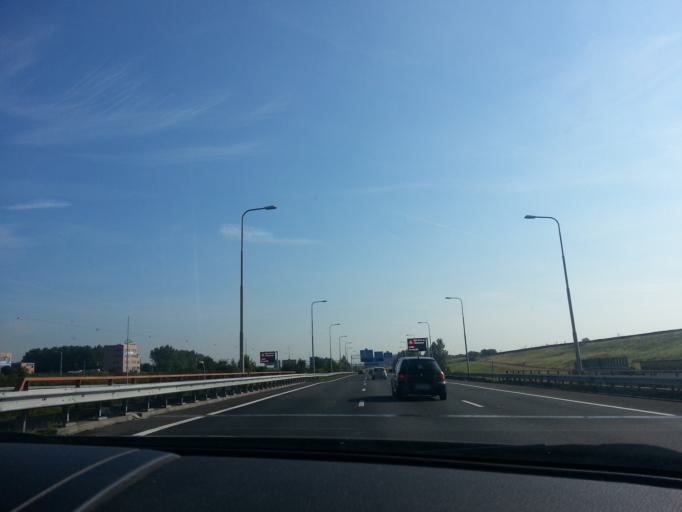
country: NL
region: South Holland
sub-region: Gemeente Den Haag
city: Ypenburg
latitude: 52.0463
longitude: 4.3568
